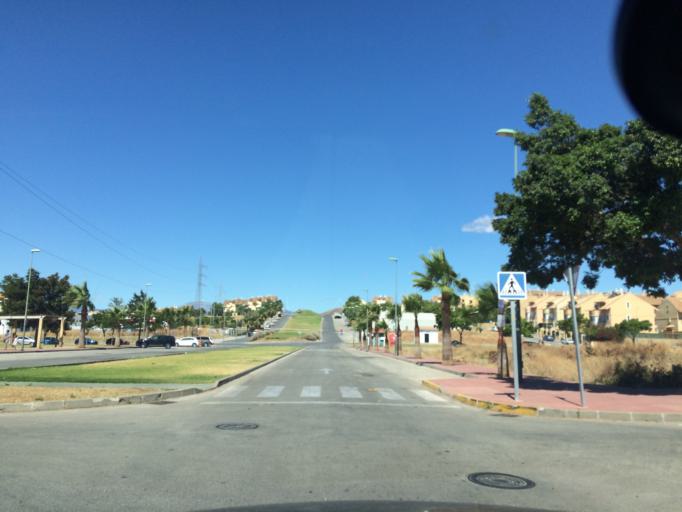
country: ES
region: Andalusia
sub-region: Provincia de Malaga
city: Estacion de Cartama
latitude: 36.7394
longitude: -4.6061
